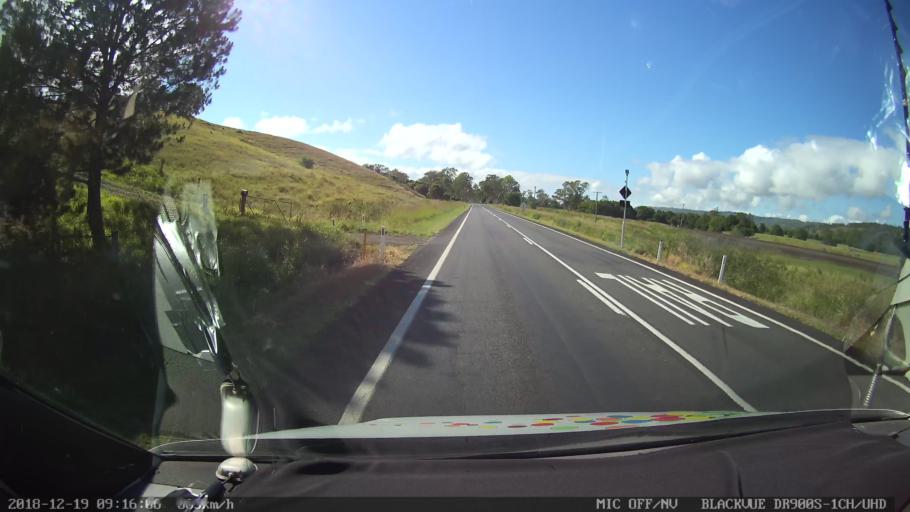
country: AU
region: New South Wales
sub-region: Kyogle
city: Kyogle
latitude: -28.5177
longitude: 152.9654
